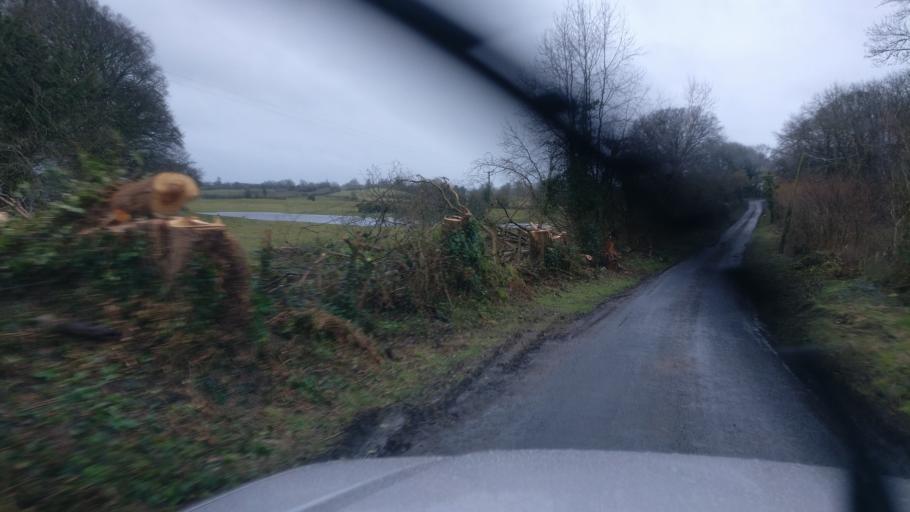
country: IE
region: Connaught
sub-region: County Galway
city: Ballinasloe
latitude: 53.2901
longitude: -8.2782
